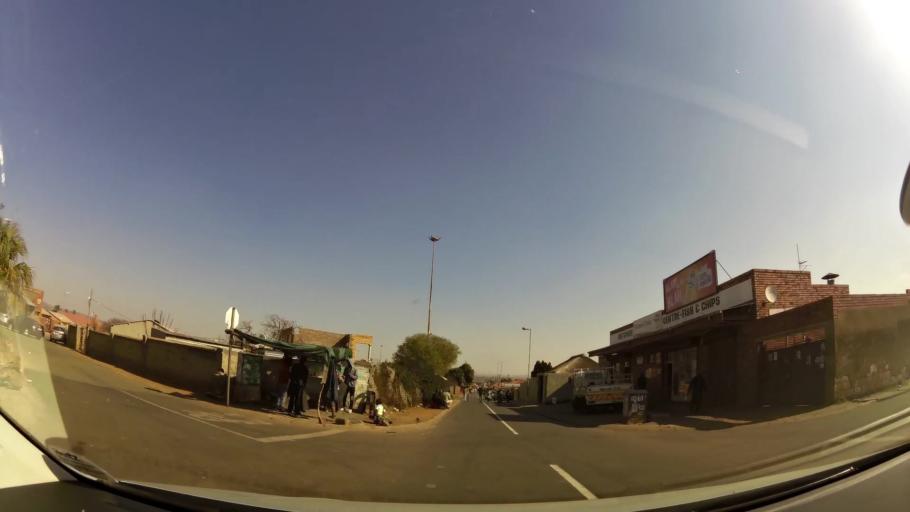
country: ZA
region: Gauteng
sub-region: City of Johannesburg Metropolitan Municipality
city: Soweto
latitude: -26.2837
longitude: 27.8577
